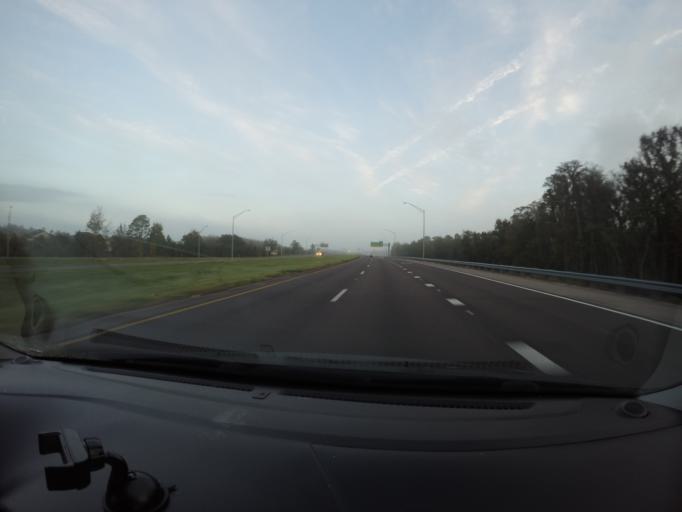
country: US
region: Florida
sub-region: Orange County
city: Conway
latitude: 28.4189
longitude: -81.2271
